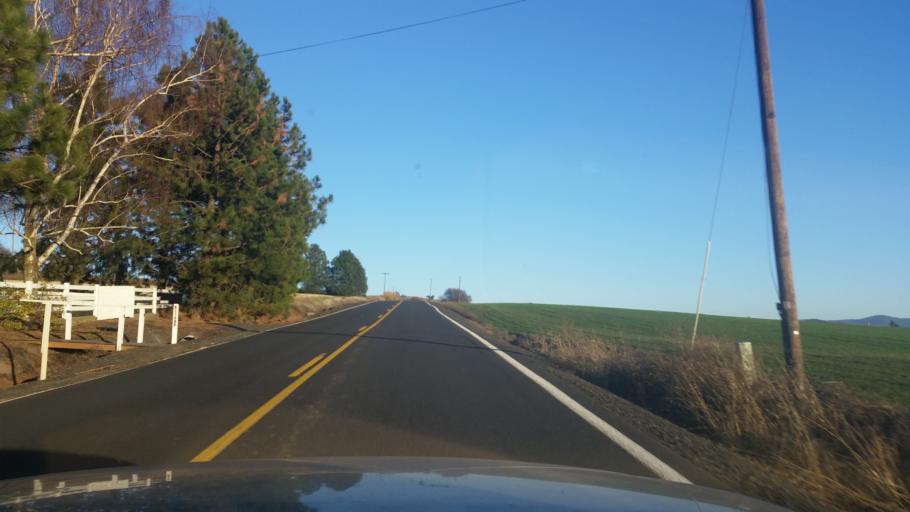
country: US
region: Washington
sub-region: Spokane County
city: Opportunity
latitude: 47.3512
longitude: -117.2447
